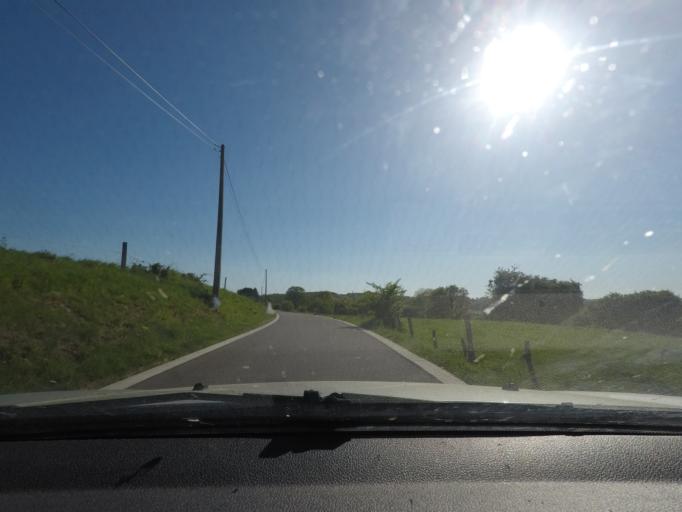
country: BE
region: Wallonia
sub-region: Province du Luxembourg
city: Tintigny
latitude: 49.7002
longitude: 5.4473
